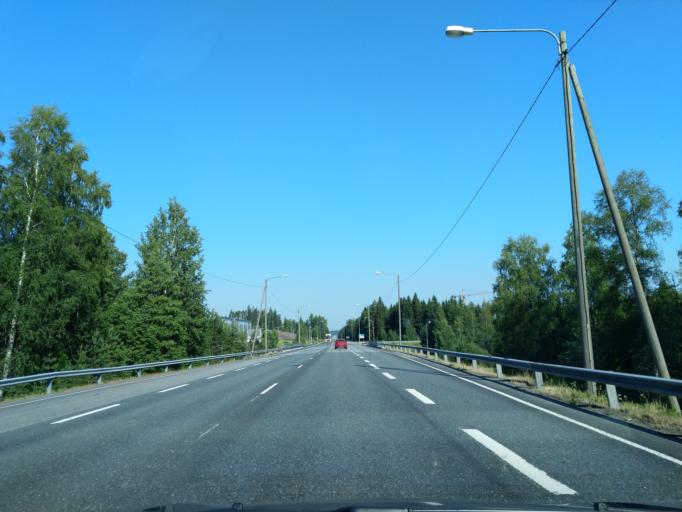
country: FI
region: Haeme
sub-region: Forssa
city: Forssa
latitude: 60.7889
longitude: 23.6495
